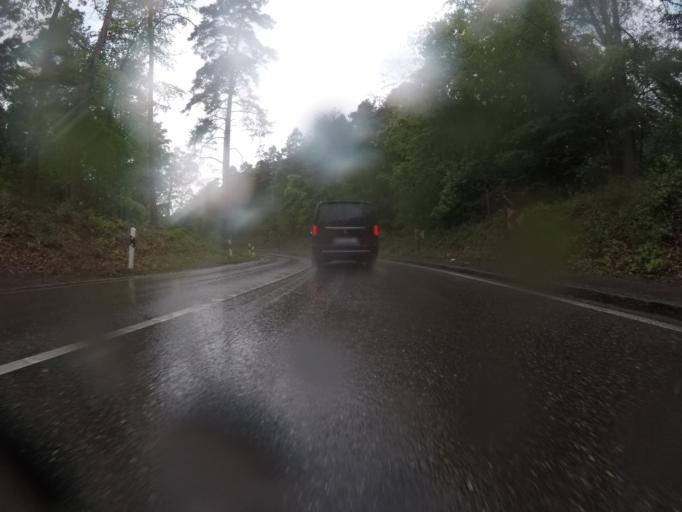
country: DE
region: Baden-Wuerttemberg
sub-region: Regierungsbezirk Stuttgart
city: Stuttgart
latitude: 48.7525
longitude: 9.1525
